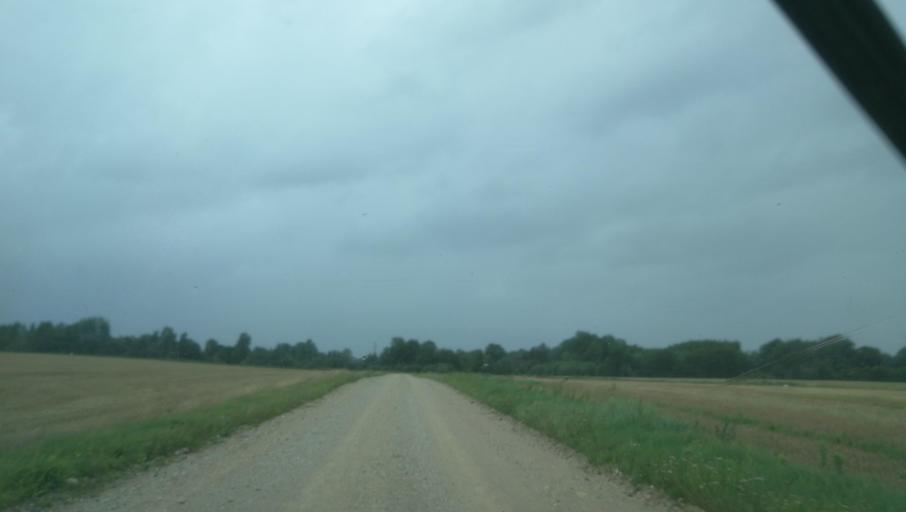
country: LV
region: Beverina
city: Murmuiza
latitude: 57.4062
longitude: 25.4625
